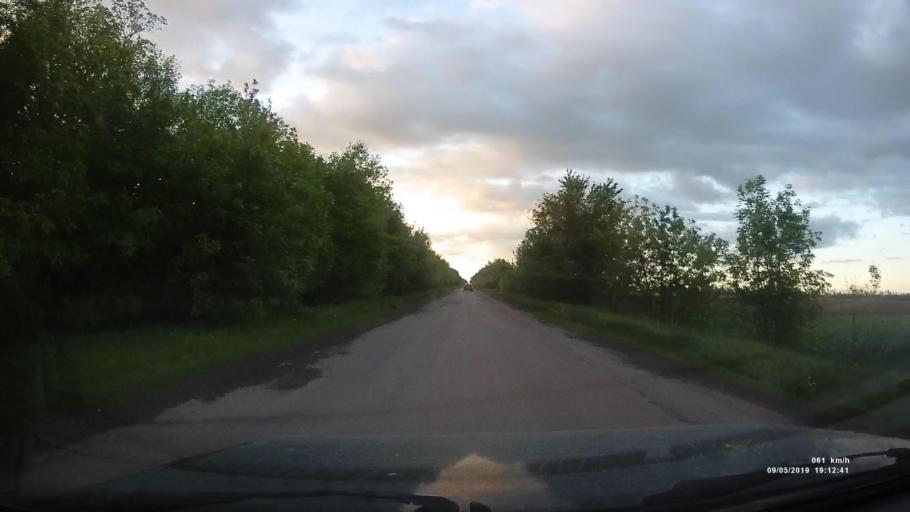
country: RU
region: Krasnodarskiy
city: Kanelovskaya
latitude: 46.7438
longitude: 39.2137
